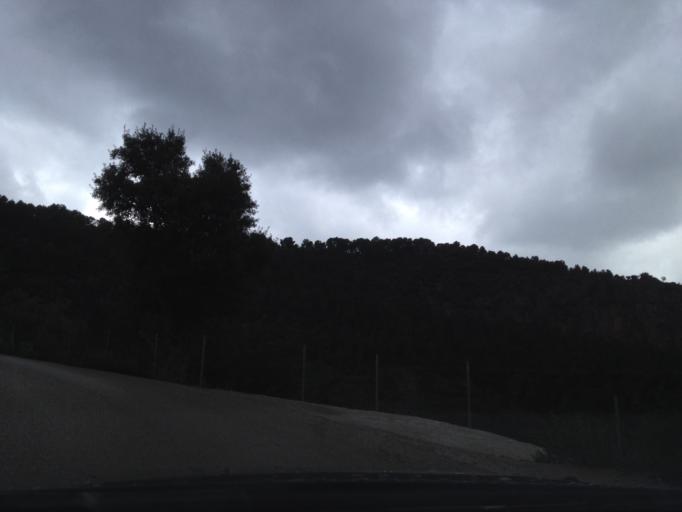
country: ES
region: Balearic Islands
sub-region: Illes Balears
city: Soller
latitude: 39.7753
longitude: 2.6869
